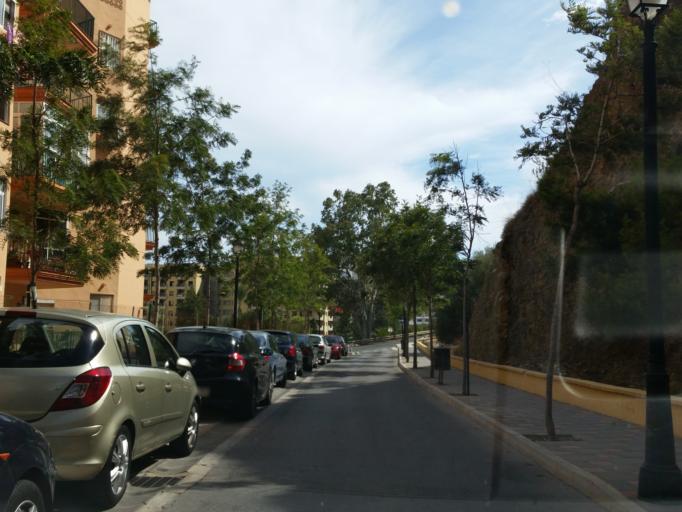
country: ES
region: Andalusia
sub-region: Provincia de Malaga
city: Fuengirola
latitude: 36.5606
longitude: -4.6090
